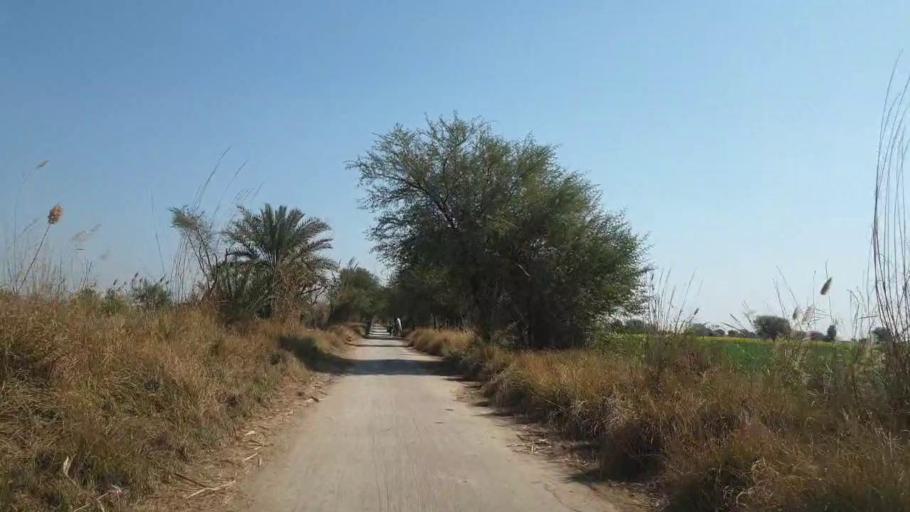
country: PK
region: Sindh
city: Mirpur Khas
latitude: 25.6447
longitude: 69.0254
